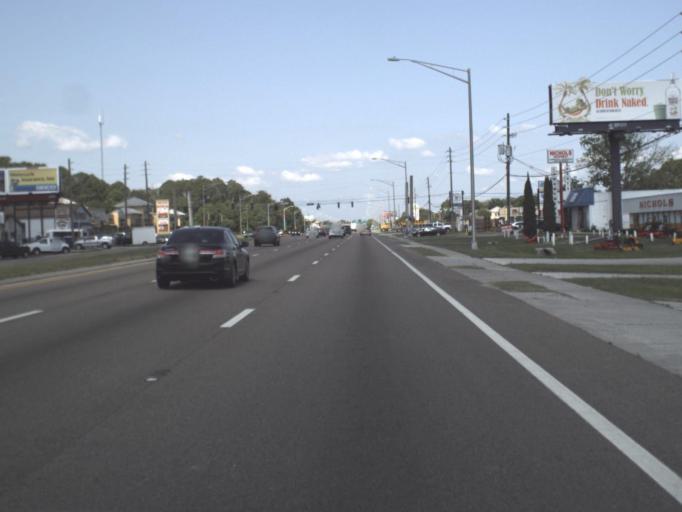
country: US
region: Florida
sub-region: Duval County
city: Jacksonville
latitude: 30.2868
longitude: -81.5466
